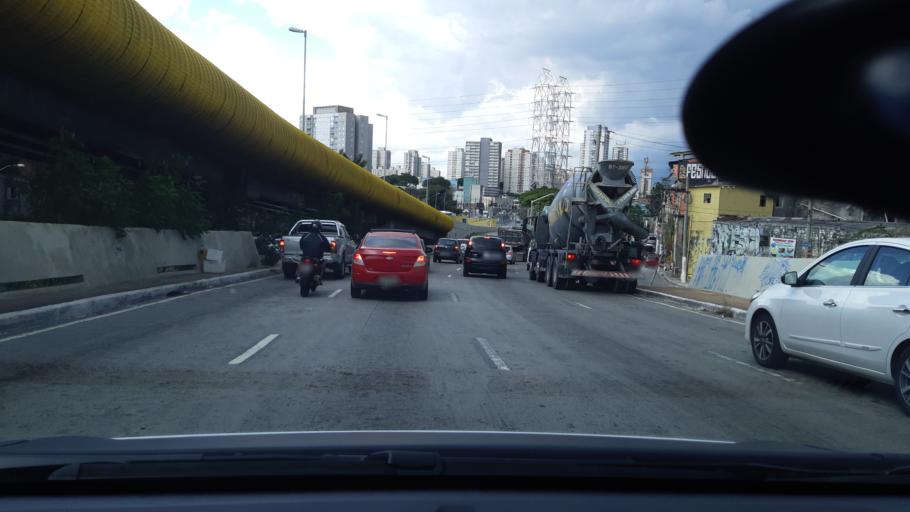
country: BR
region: Sao Paulo
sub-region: Sao Caetano Do Sul
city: Sao Caetano do Sul
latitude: -23.5869
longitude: -46.5904
